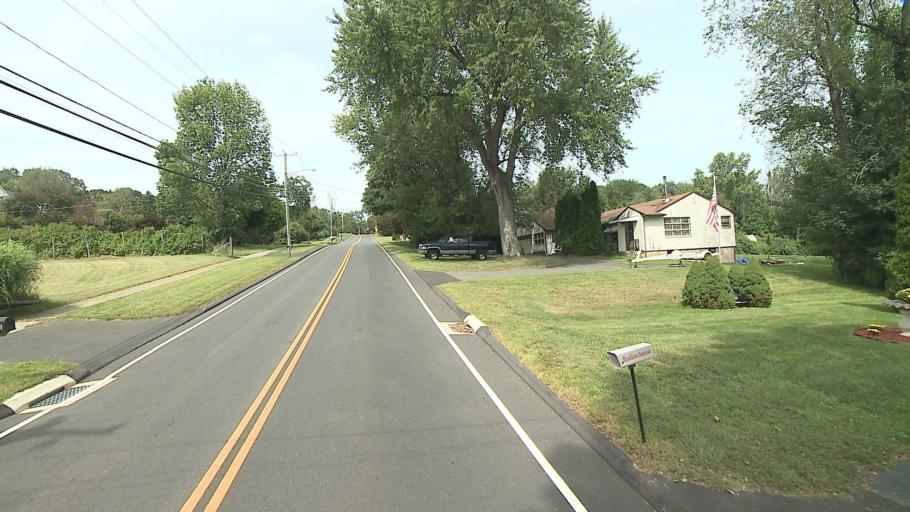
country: US
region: Connecticut
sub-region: Litchfield County
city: Plymouth
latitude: 41.6555
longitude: -73.0515
